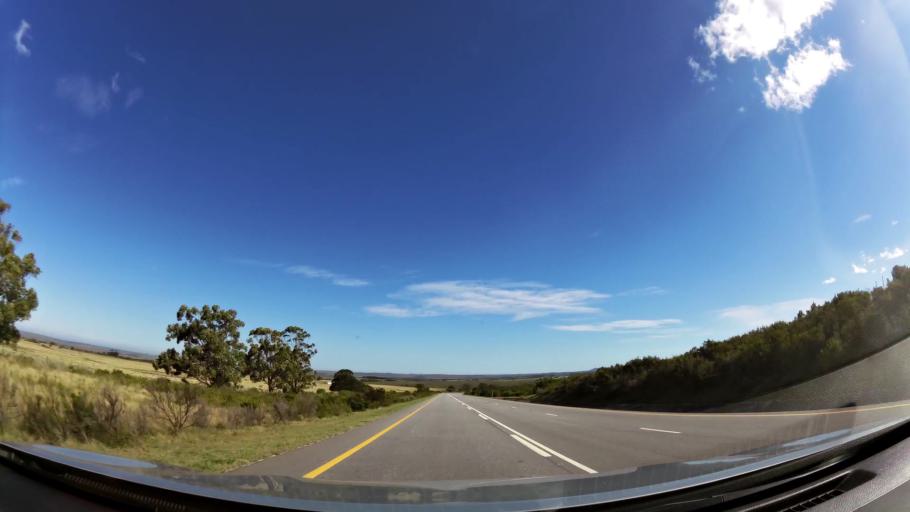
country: ZA
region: Eastern Cape
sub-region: Cacadu District Municipality
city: Kruisfontein
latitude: -34.0027
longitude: 24.6802
